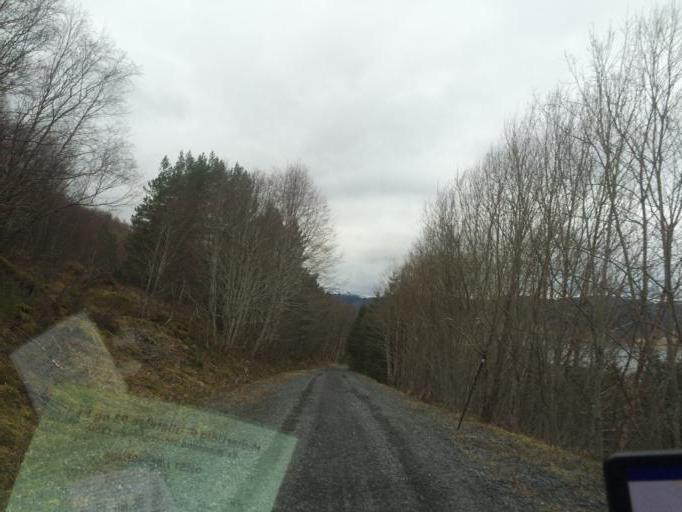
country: NO
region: More og Romsdal
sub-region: Gjemnes
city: Batnfjordsora
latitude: 62.9662
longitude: 7.7291
